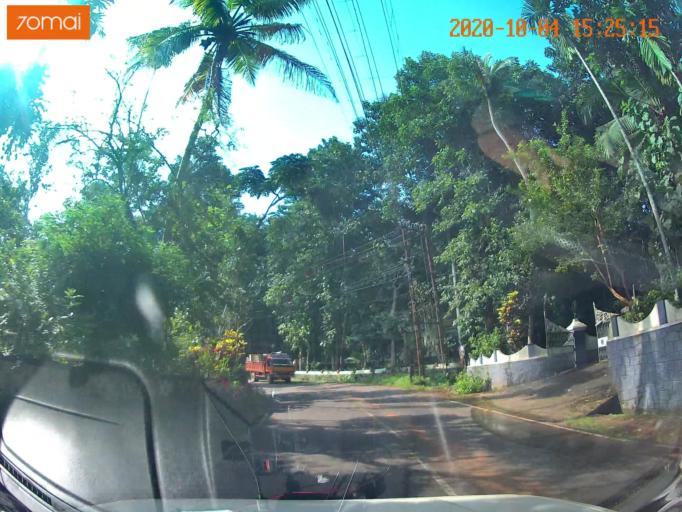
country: IN
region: Kerala
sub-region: Kottayam
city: Palackattumala
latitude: 9.7225
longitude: 76.6497
